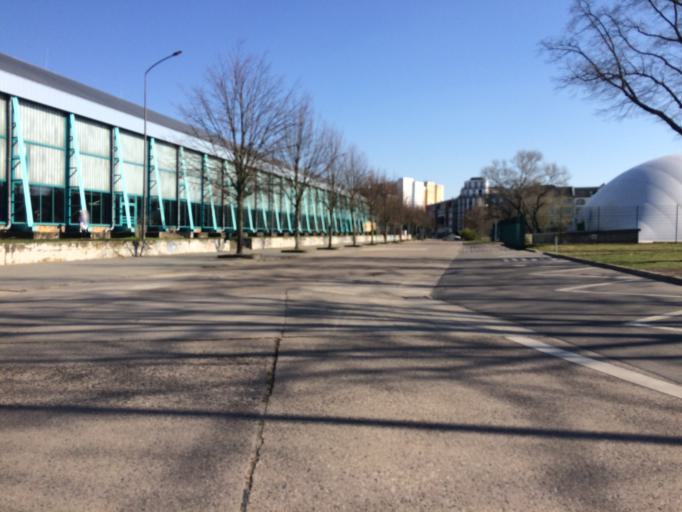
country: DE
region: Berlin
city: Fennpfuhl
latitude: 52.5402
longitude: 13.4795
